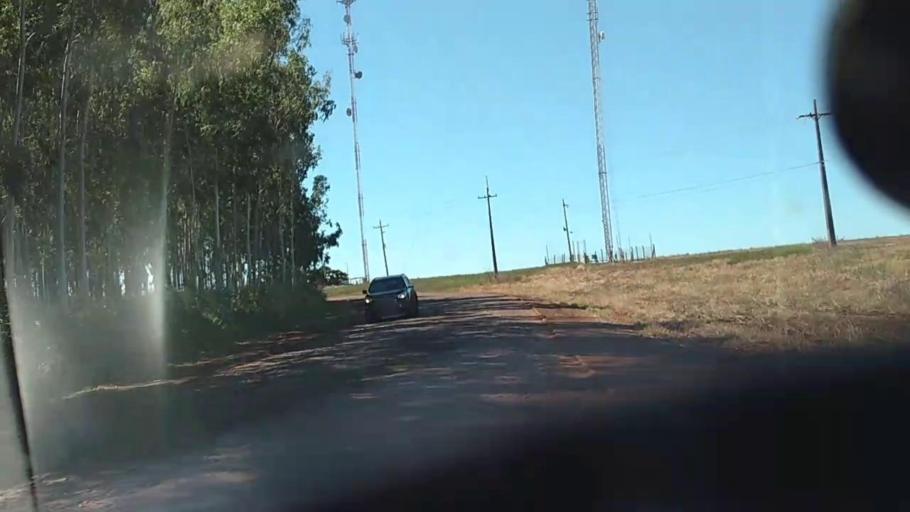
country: PY
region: Alto Parana
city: Naranjal
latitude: -25.9768
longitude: -55.1601
